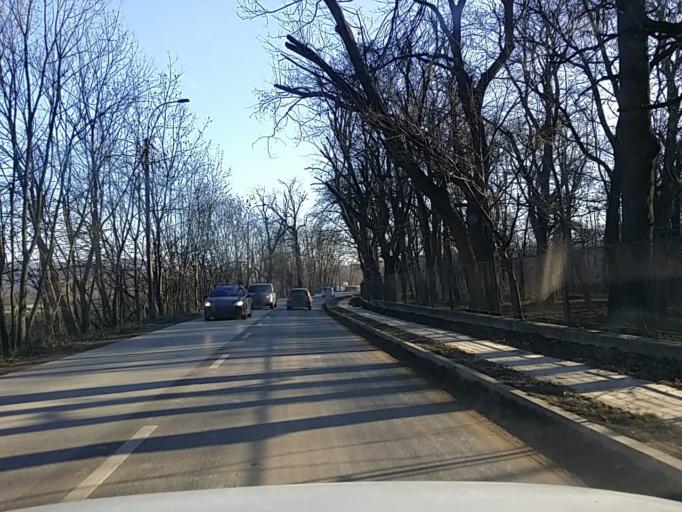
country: HU
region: Pest
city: Pilisszentivan
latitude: 47.5739
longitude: 18.8954
